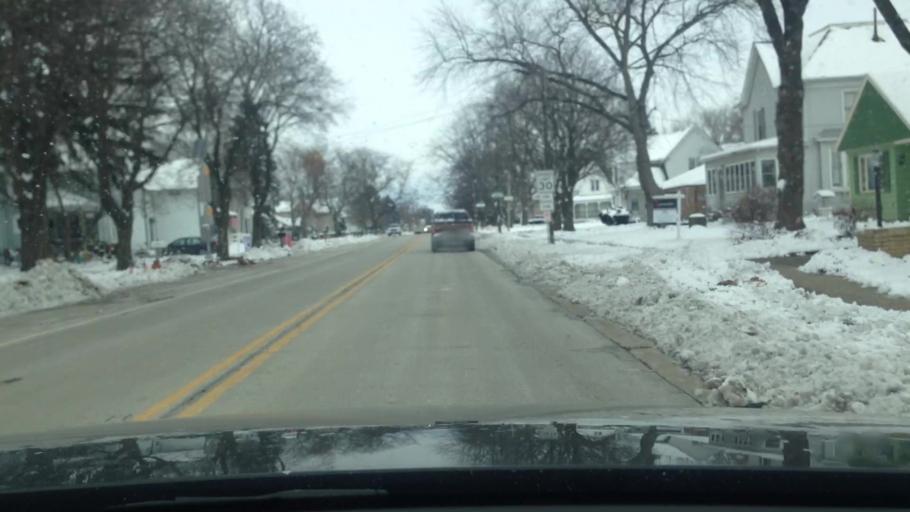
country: US
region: Illinois
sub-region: McHenry County
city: Hebron
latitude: 42.4664
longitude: -88.4328
